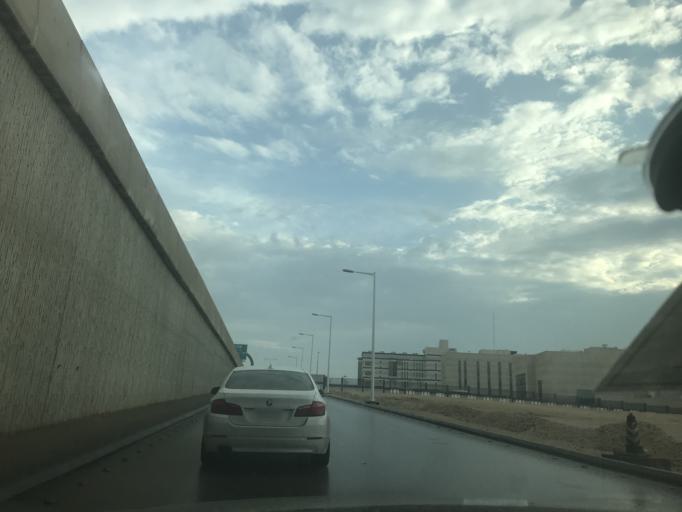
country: SA
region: Ar Riyad
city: Riyadh
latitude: 24.7377
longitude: 46.7458
